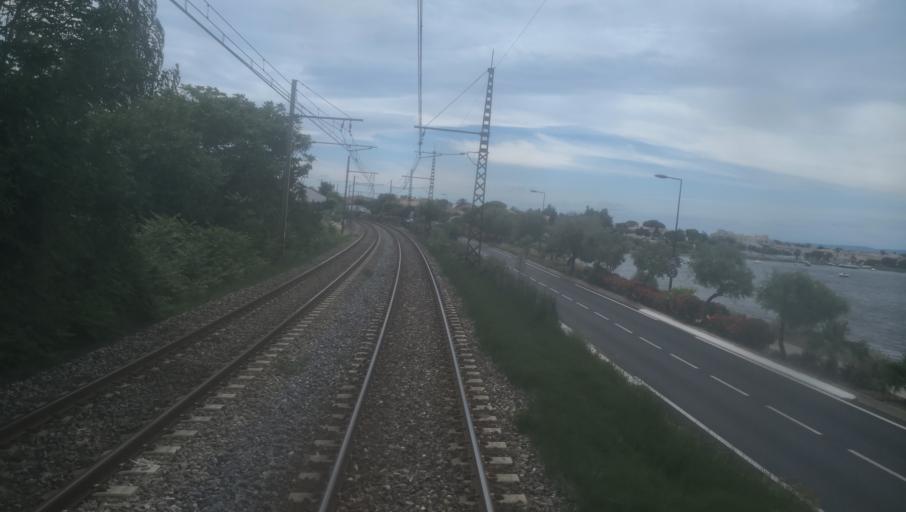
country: FR
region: Languedoc-Roussillon
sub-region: Departement de l'Herault
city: Sete
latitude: 43.4144
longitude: 3.6746
